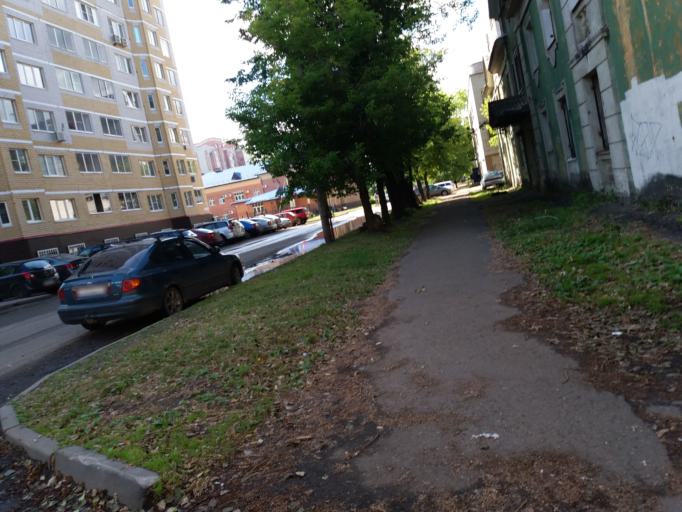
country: RU
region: Jaroslavl
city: Yaroslavl
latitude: 57.6419
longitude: 39.8397
